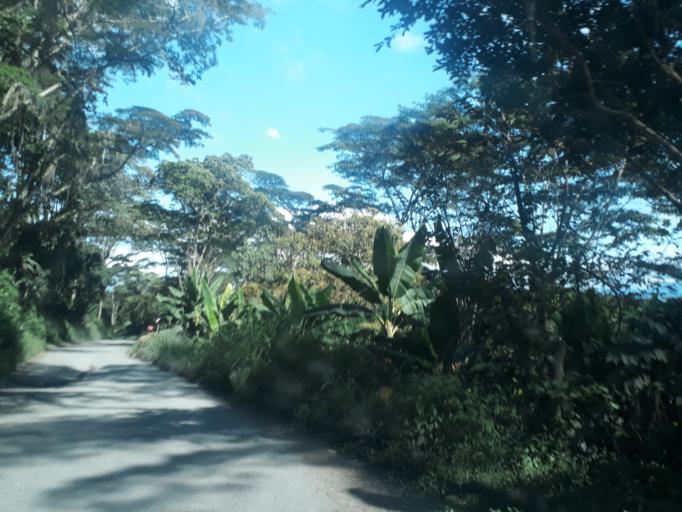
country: CO
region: Santander
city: Velez
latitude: 6.0534
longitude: -73.6493
